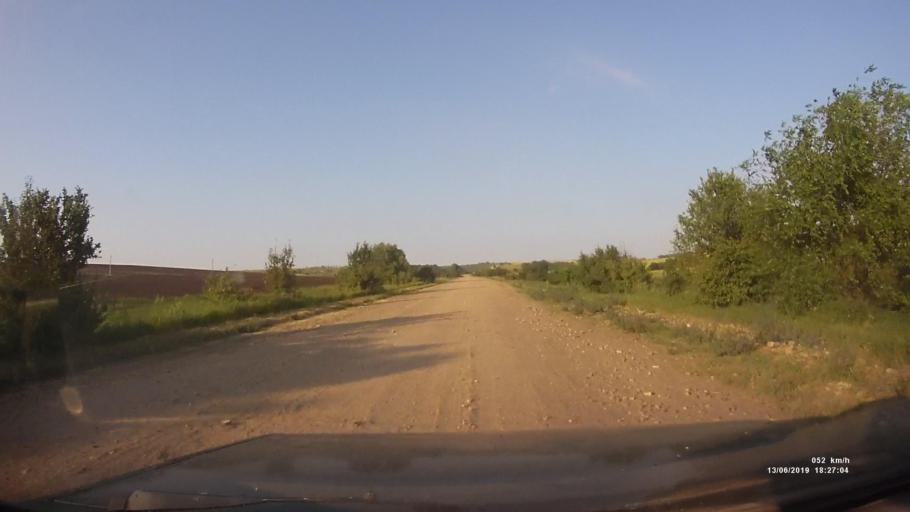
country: RU
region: Rostov
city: Kazanskaya
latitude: 49.8529
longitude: 41.3192
